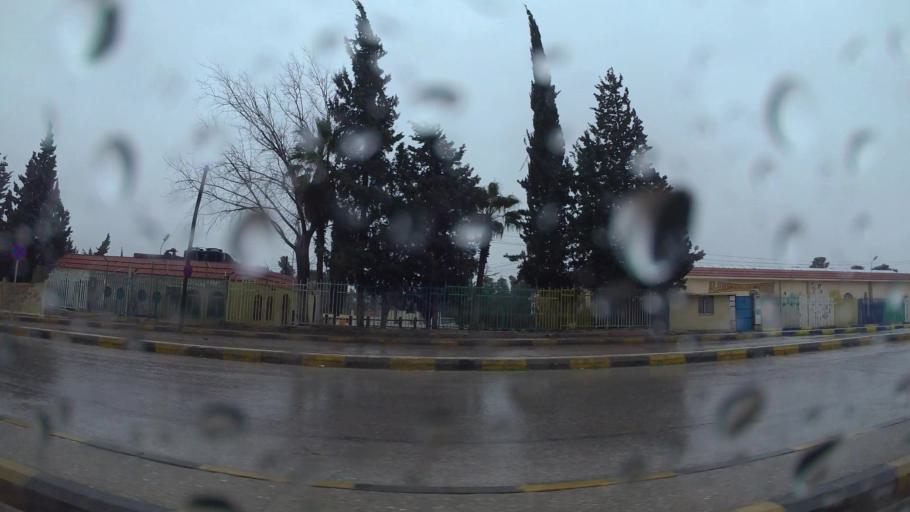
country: JO
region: Amman
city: Al Jubayhah
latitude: 32.0470
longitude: 35.8735
